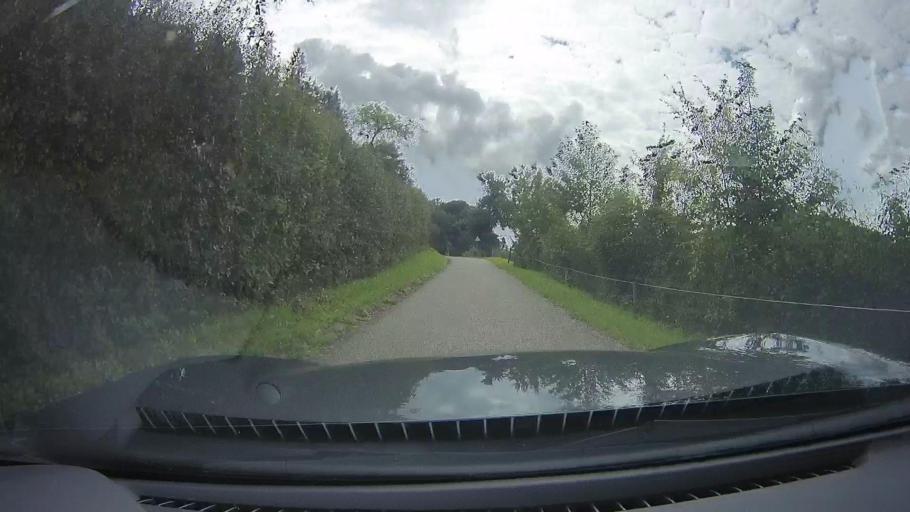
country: DE
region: Baden-Wuerttemberg
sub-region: Regierungsbezirk Stuttgart
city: Kaisersbach
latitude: 48.9585
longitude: 9.6414
